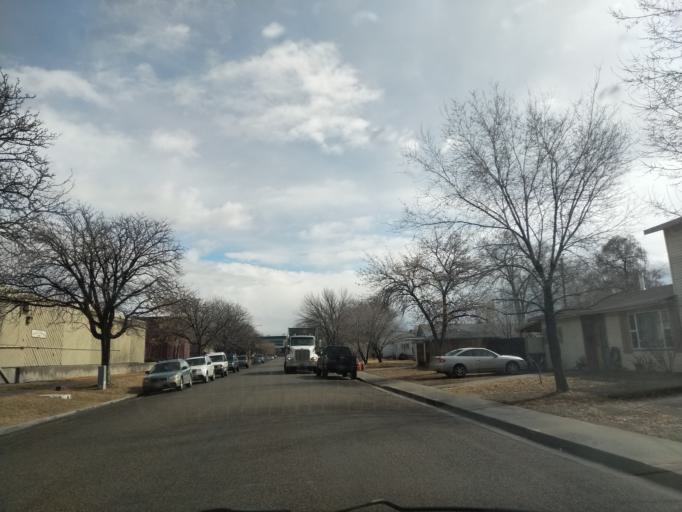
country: US
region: Colorado
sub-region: Mesa County
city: Grand Junction
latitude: 39.0764
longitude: -108.5576
